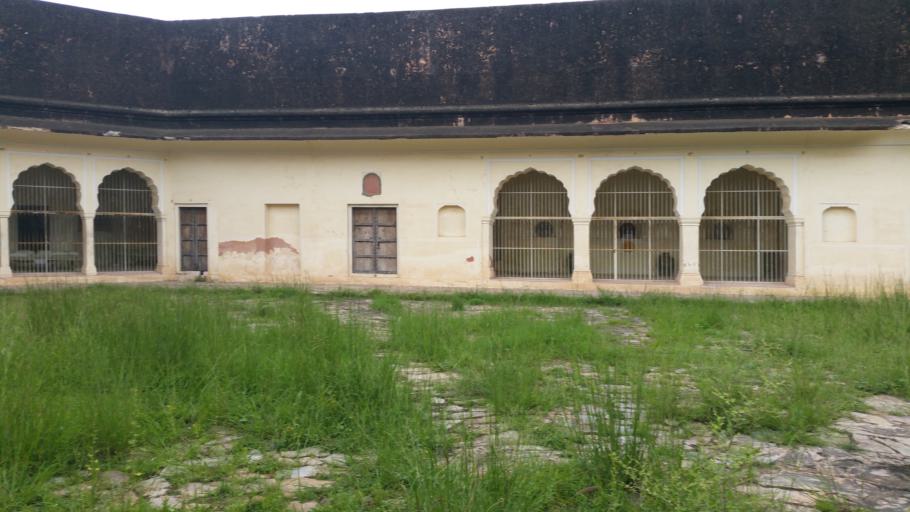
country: IN
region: Rajasthan
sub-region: Jaipur
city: Jaipur
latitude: 26.9845
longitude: 75.8458
